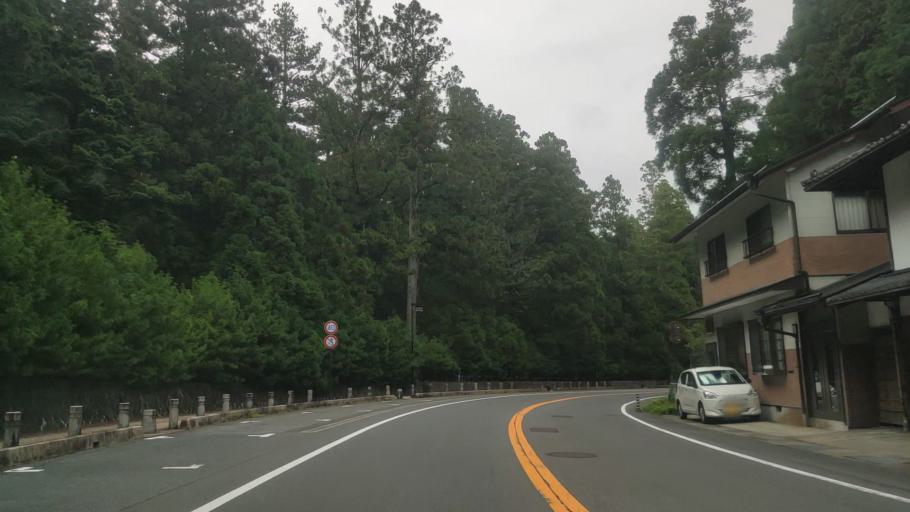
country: JP
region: Wakayama
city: Koya
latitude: 34.2155
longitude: 135.5986
